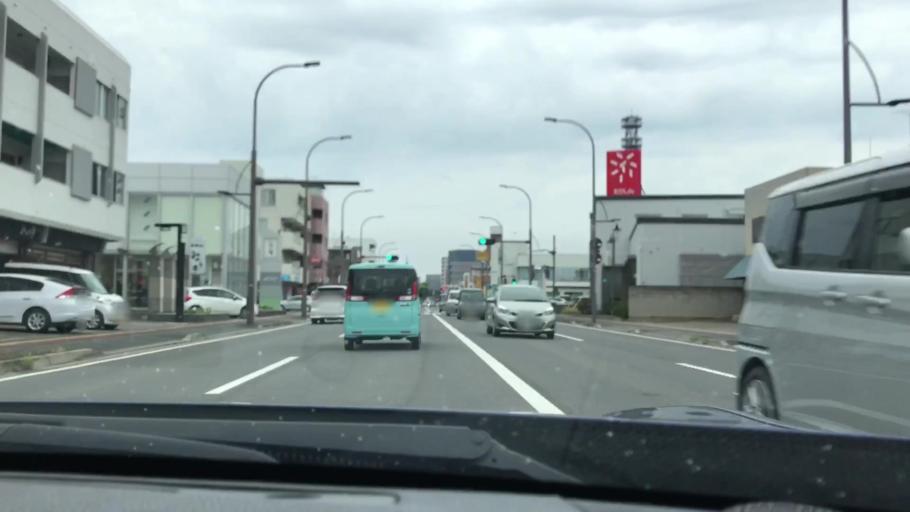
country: JP
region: Gunma
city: Maebashi-shi
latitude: 36.3783
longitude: 139.0696
